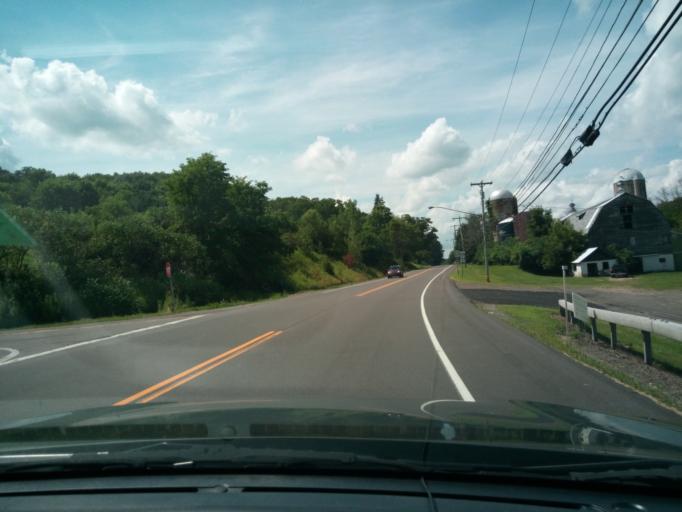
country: US
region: New York
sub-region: Chemung County
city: Southport
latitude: 42.0175
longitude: -76.7324
